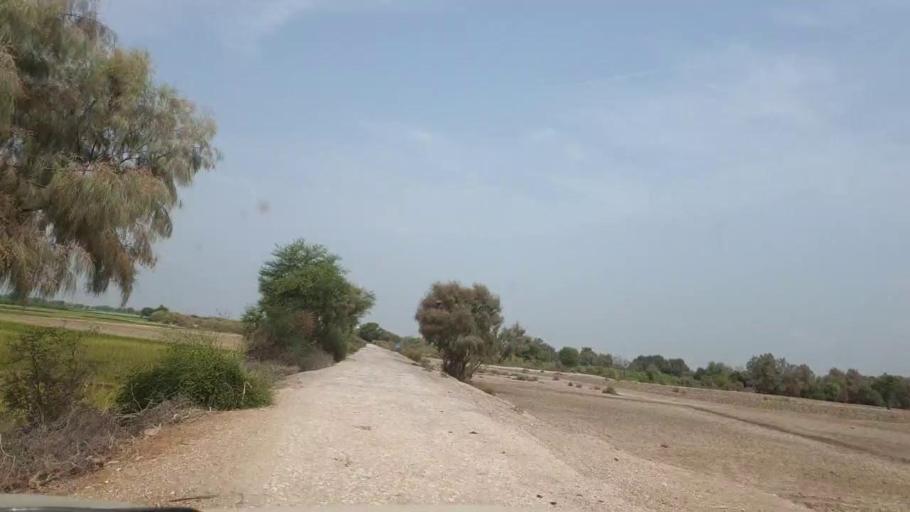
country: PK
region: Sindh
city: Sobhadero
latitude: 27.3933
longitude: 68.2645
